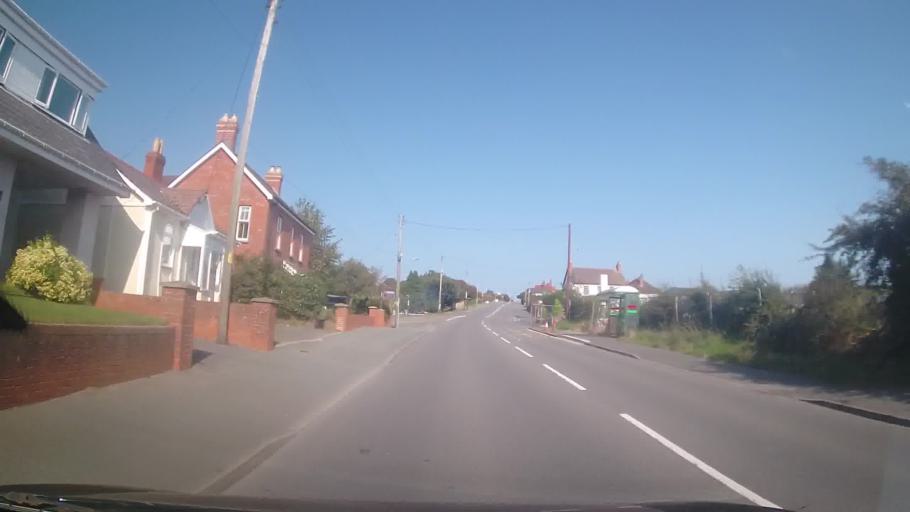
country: GB
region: Wales
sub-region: County of Ceredigion
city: Cardigan
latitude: 52.0985
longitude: -4.6182
